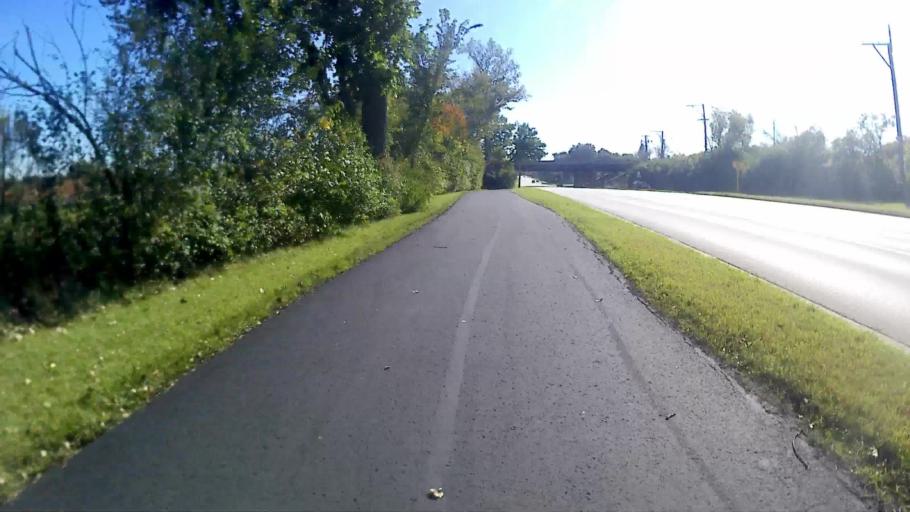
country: US
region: Illinois
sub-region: DuPage County
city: Addison
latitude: 41.9441
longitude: -87.9886
